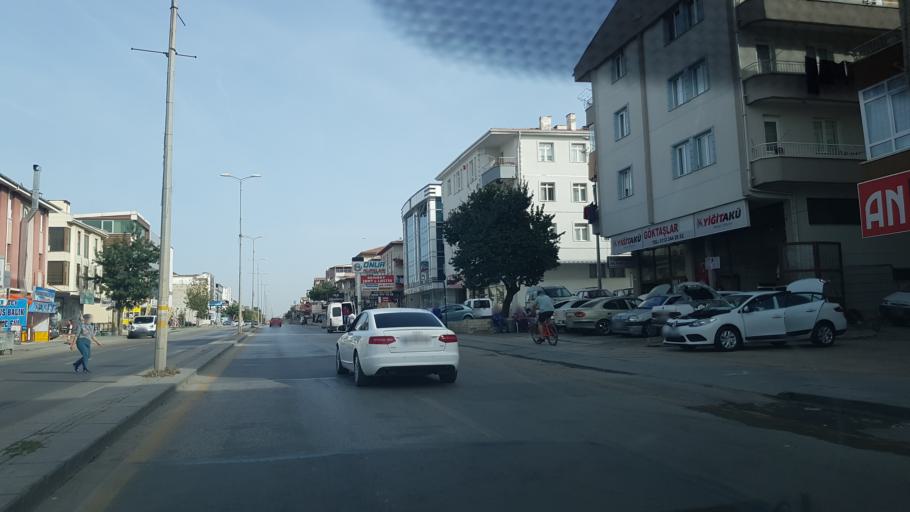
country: TR
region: Ankara
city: Etimesgut
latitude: 39.9504
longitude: 32.6531
